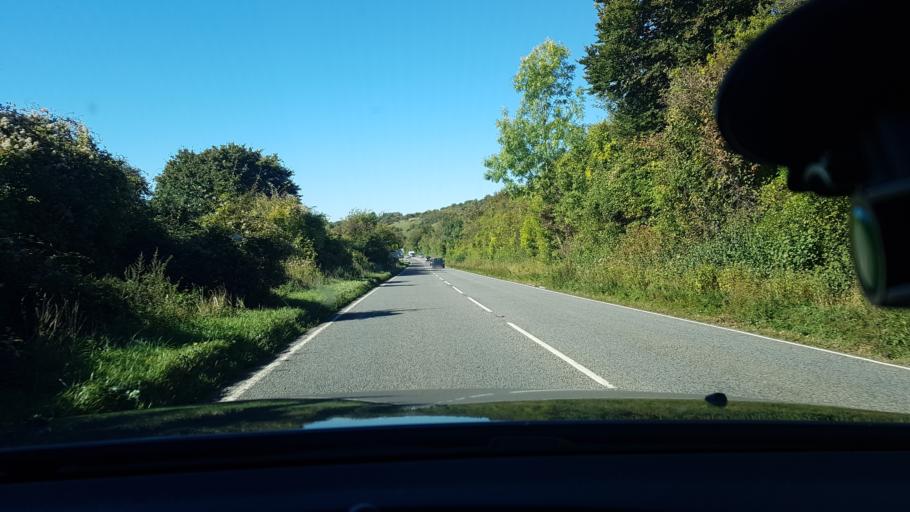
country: GB
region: England
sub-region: Hampshire
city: Kings Worthy
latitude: 51.0583
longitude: -1.2789
